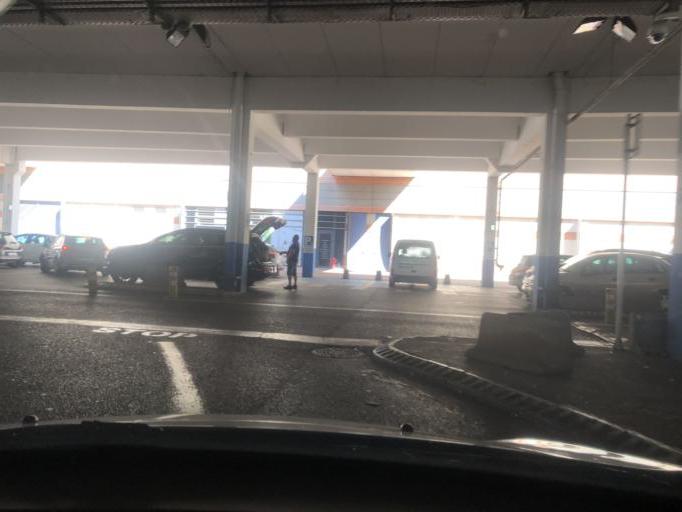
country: FR
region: Provence-Alpes-Cote d'Azur
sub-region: Departement des Bouches-du-Rhone
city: Marseille 15
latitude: 43.3632
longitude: 5.3496
